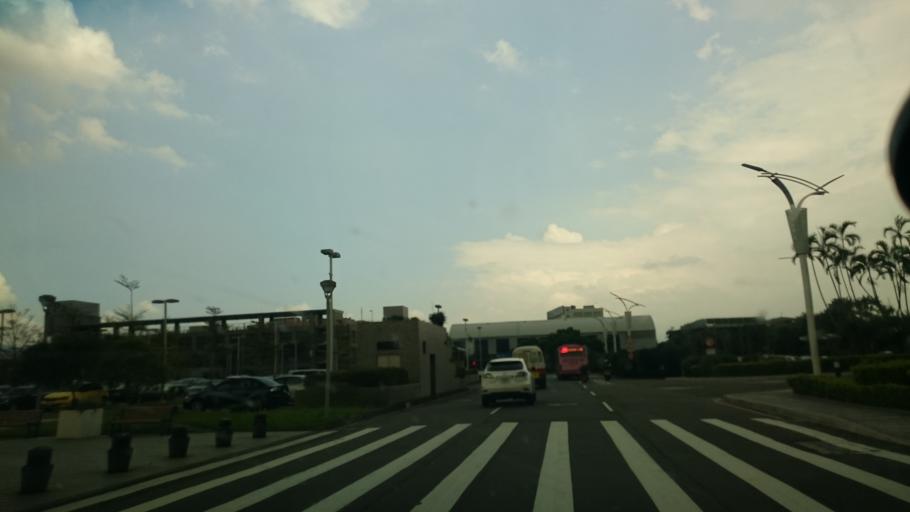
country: TW
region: Taipei
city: Taipei
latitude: 25.0623
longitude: 121.5520
